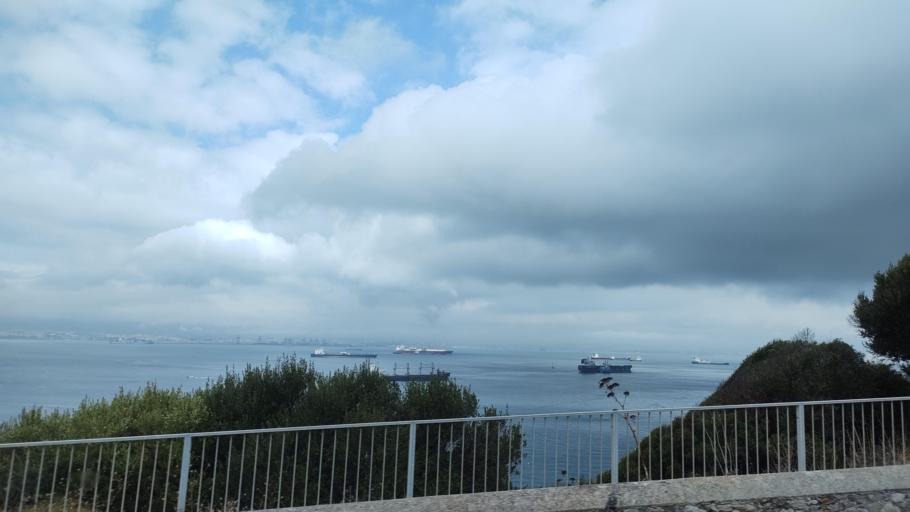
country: GI
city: Gibraltar
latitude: 36.1149
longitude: -5.3483
